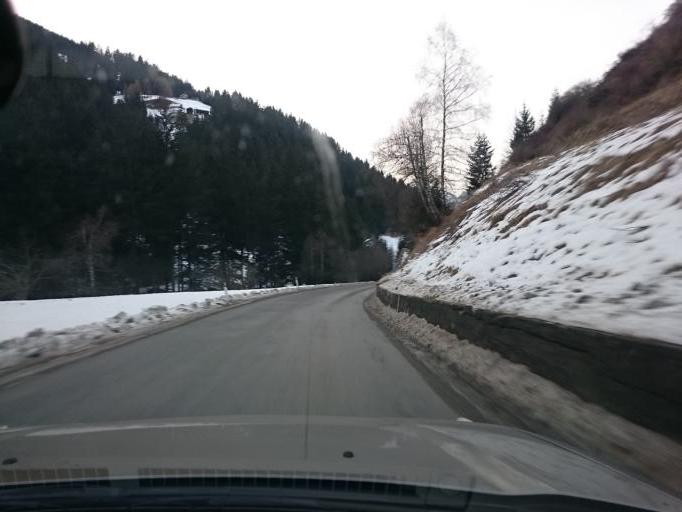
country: IT
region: Lombardy
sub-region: Provincia di Sondrio
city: Sant'Antonio
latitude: 46.4527
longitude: 10.4342
